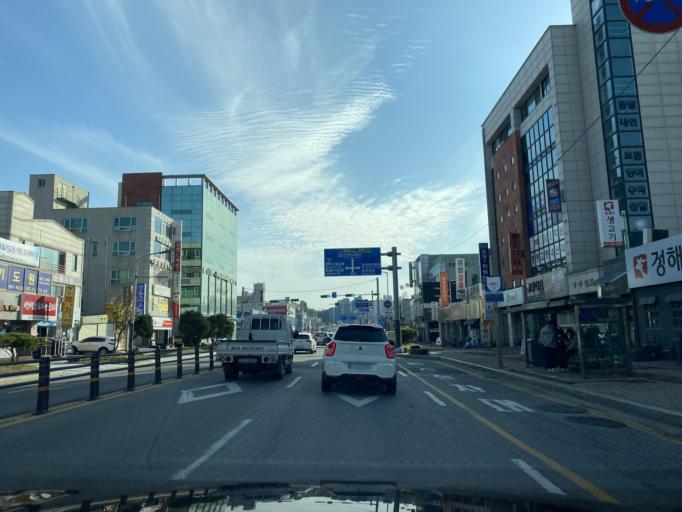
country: KR
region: Chungcheongnam-do
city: Cheonan
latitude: 36.8007
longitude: 127.1591
